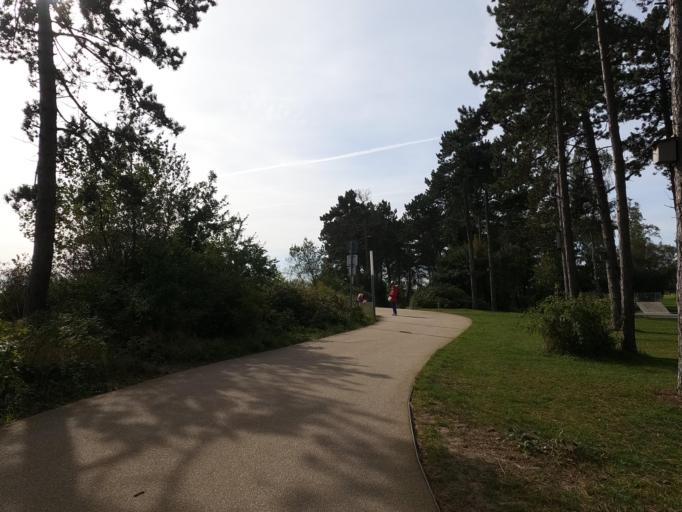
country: DE
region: Schleswig-Holstein
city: Kellenhusen
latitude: 54.1839
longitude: 11.0578
